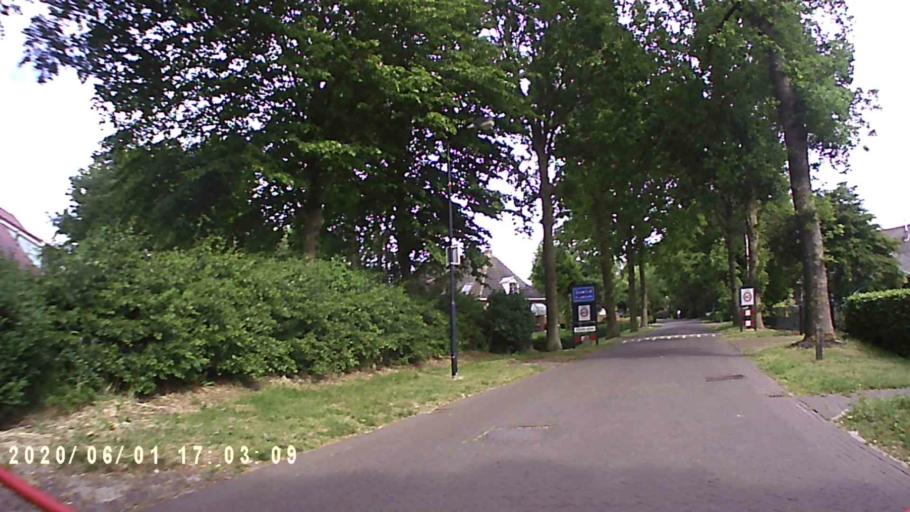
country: NL
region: Friesland
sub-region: Gemeente Tytsjerksteradiel
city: Hurdegaryp
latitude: 53.1773
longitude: 5.9294
